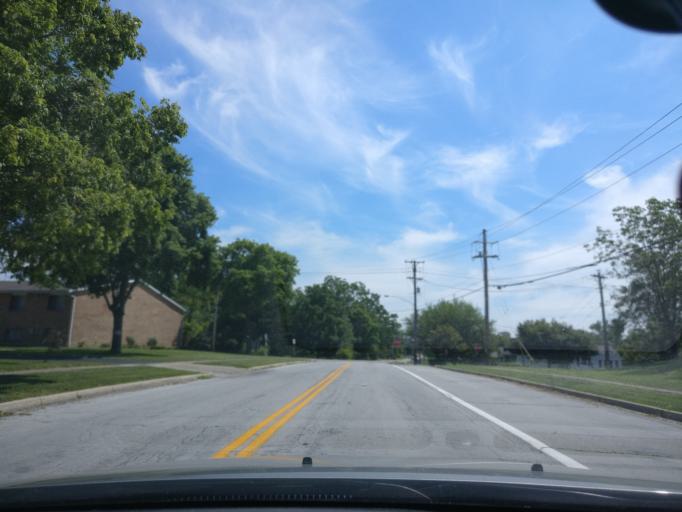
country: US
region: Ohio
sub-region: Montgomery County
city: West Carrollton City
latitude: 39.6417
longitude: -84.2550
